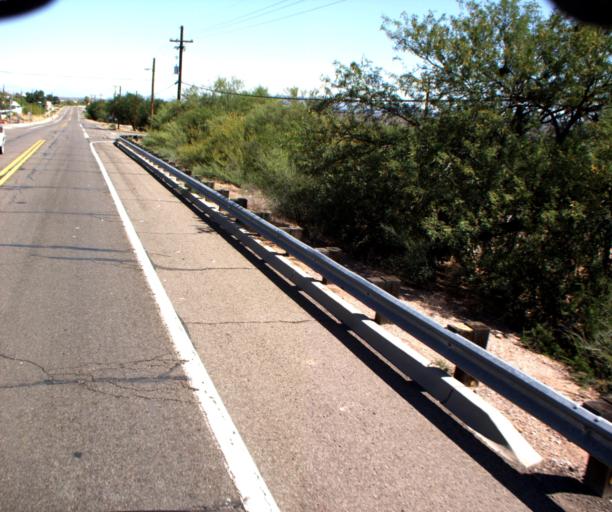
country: US
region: Arizona
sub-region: Pinal County
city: Mammoth
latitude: 32.7298
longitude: -110.6470
